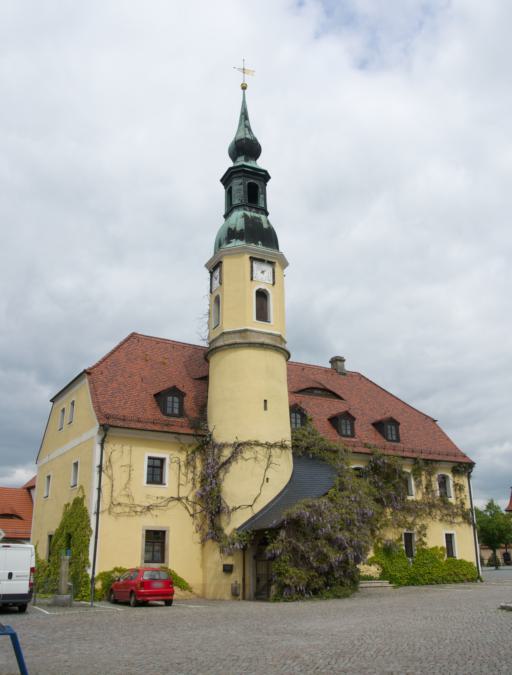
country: DE
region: Saxony
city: Weissenberg
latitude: 51.1968
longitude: 14.6582
